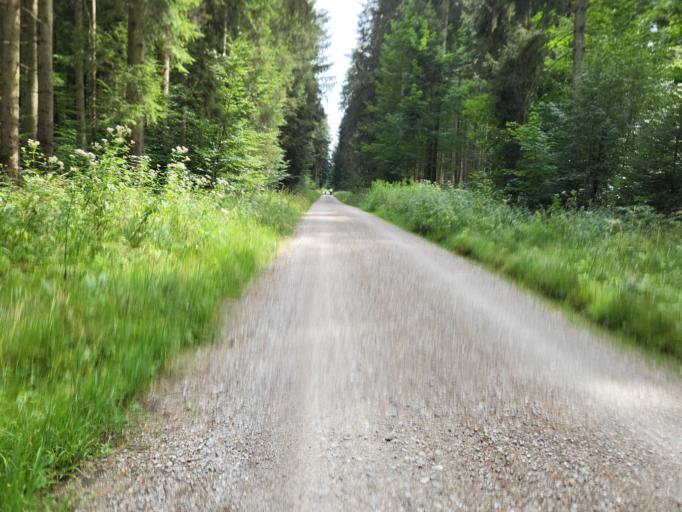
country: DE
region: Bavaria
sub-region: Upper Bavaria
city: Aying
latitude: 47.9983
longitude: 11.7568
